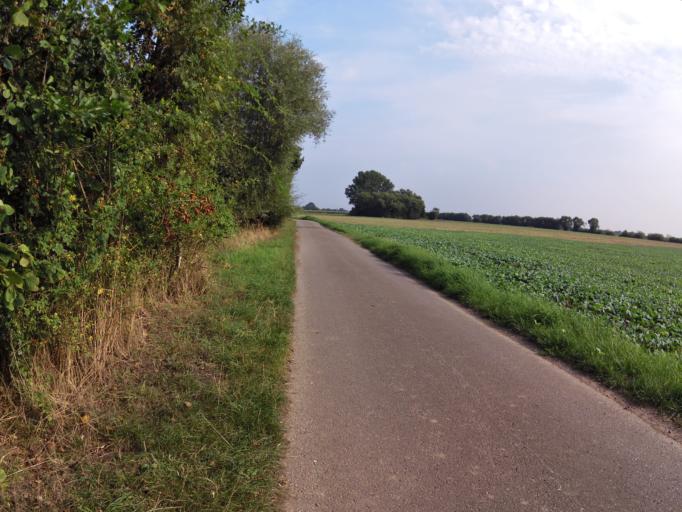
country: DE
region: Lower Saxony
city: Raddestorf
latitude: 52.4633
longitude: 9.0175
